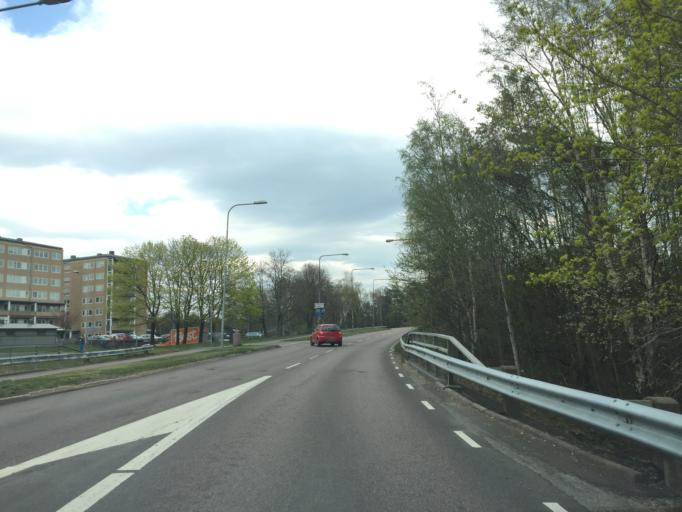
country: SE
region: Vaestra Goetaland
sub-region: Goteborg
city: Rannebergen
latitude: 57.8000
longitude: 12.0742
